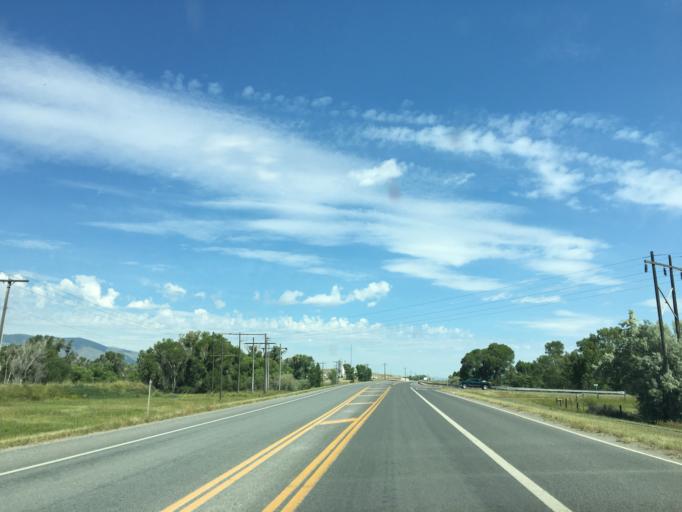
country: US
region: Montana
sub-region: Broadwater County
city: Townsend
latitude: 46.3313
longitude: -111.5295
